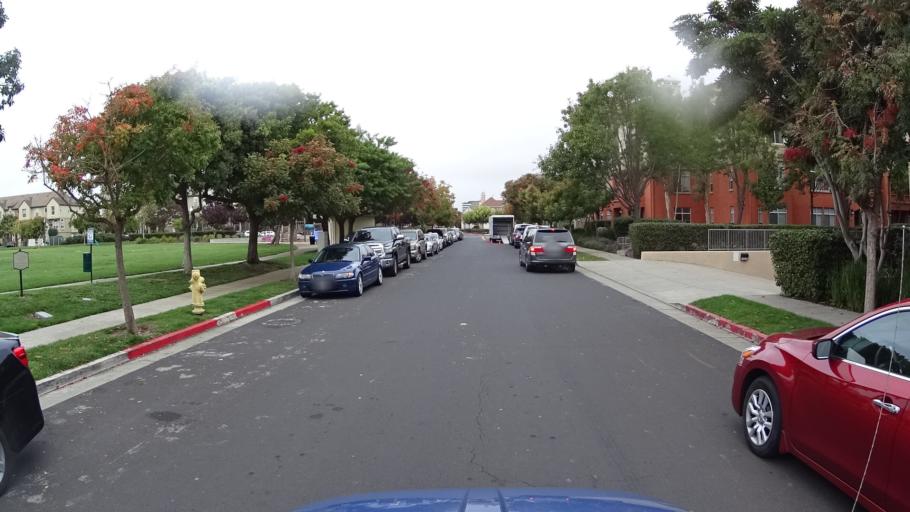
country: US
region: California
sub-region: San Mateo County
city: Foster City
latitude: 37.5461
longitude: -122.2925
